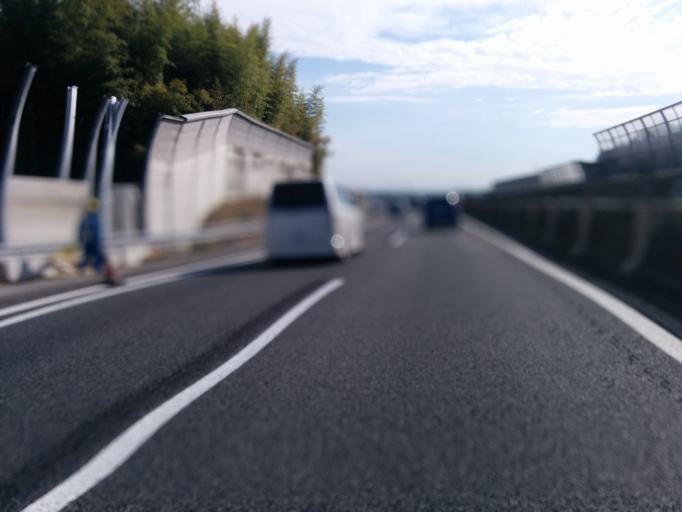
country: JP
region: Mie
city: Komono
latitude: 34.9859
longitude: 136.5419
